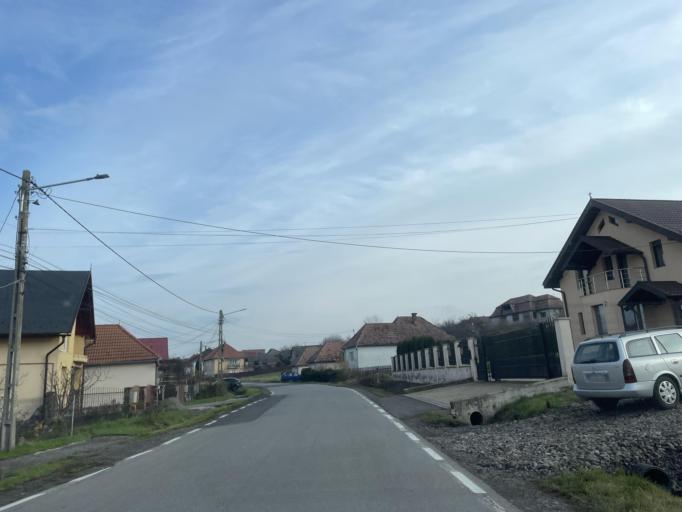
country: RO
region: Mures
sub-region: Comuna Solovastru
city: Solovastru
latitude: 46.7761
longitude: 24.7534
